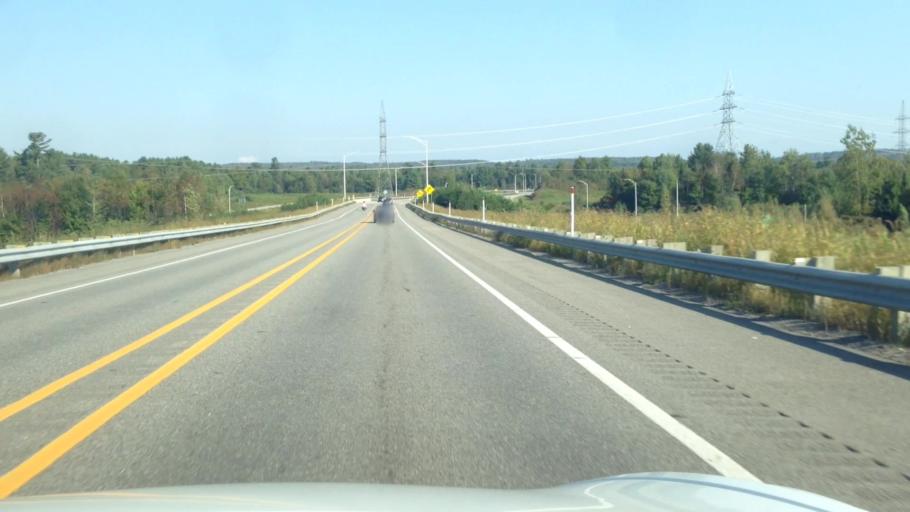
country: CA
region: Ontario
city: Clarence-Rockland
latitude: 45.6049
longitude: -75.3876
